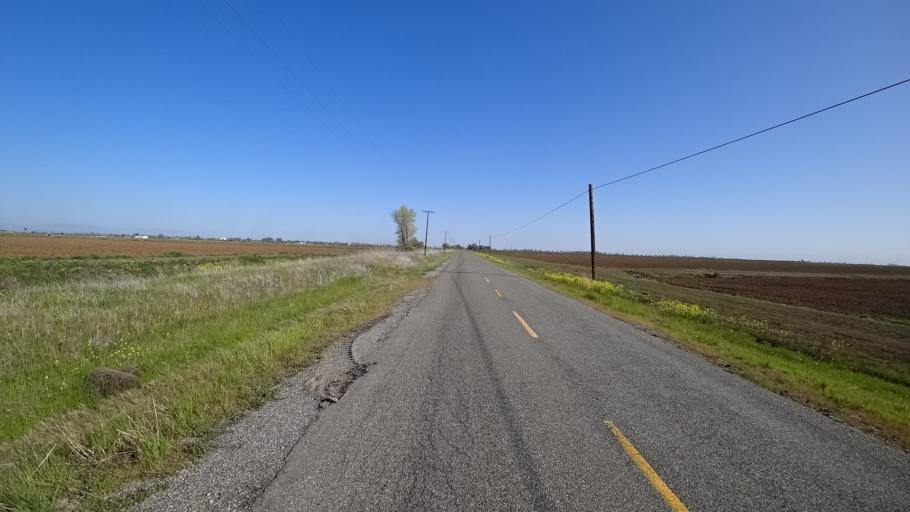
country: US
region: California
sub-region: Glenn County
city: Willows
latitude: 39.4965
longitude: -122.1745
